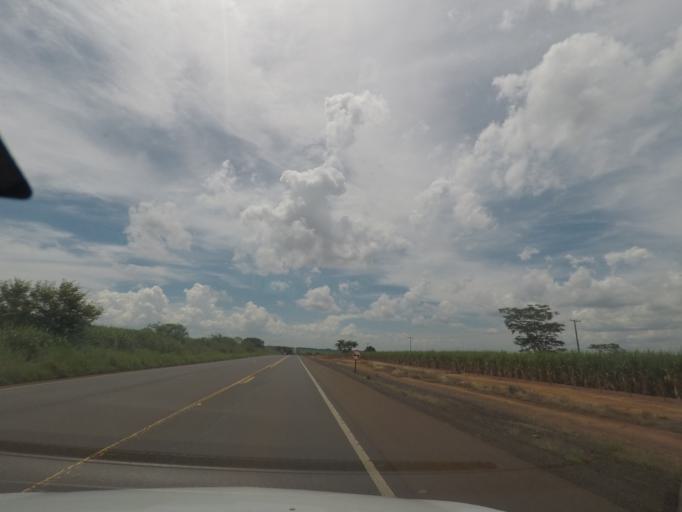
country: BR
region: Sao Paulo
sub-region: Barretos
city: Barretos
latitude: -20.3818
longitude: -48.6423
